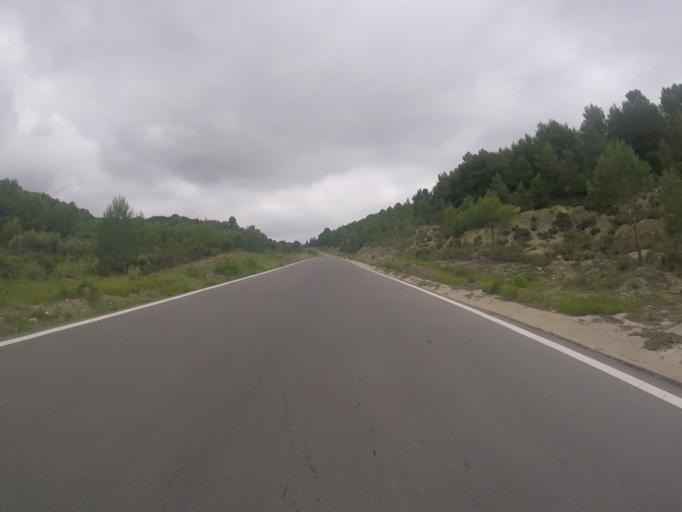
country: ES
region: Valencia
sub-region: Provincia de Castello
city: Cabanes
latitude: 40.1188
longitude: 0.0473
